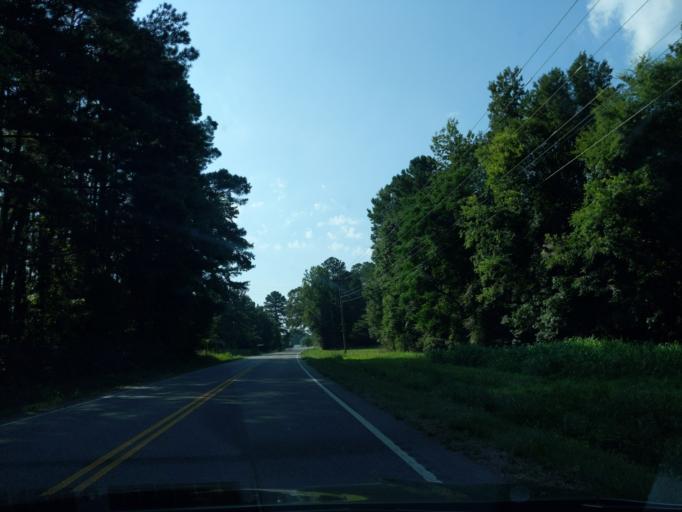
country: US
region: South Carolina
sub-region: Lexington County
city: Leesville
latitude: 34.0449
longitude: -81.5472
